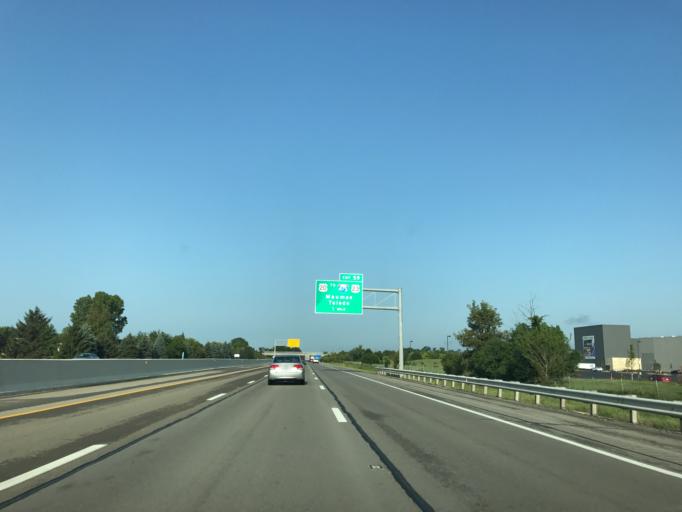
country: US
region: Ohio
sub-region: Lucas County
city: Maumee
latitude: 41.5909
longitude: -83.6474
